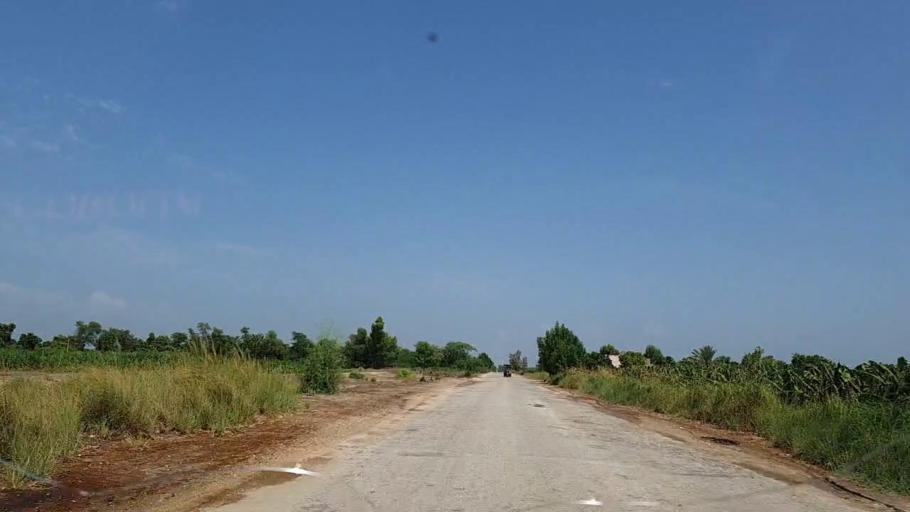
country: PK
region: Sindh
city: Naushahro Firoz
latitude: 26.8208
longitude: 68.1680
